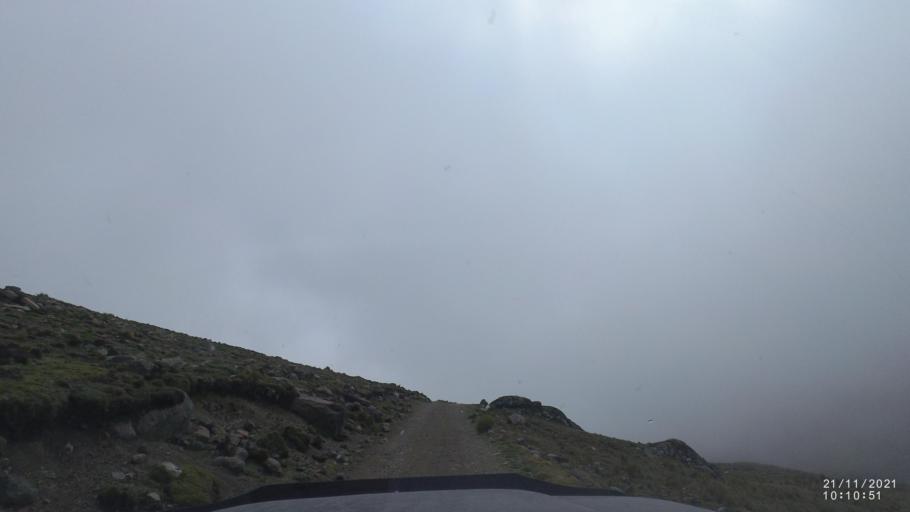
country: BO
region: Cochabamba
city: Cochabamba
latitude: -16.9956
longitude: -66.2720
